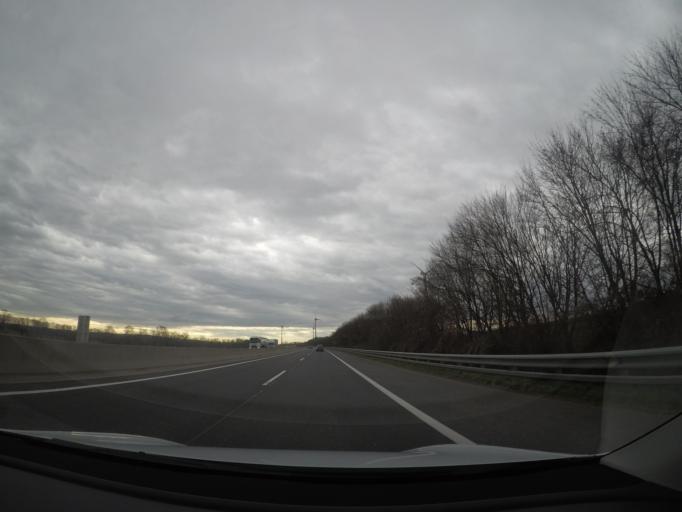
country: AT
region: Lower Austria
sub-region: Politischer Bezirk Baden
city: Ebreichsdorf
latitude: 47.9538
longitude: 16.3668
